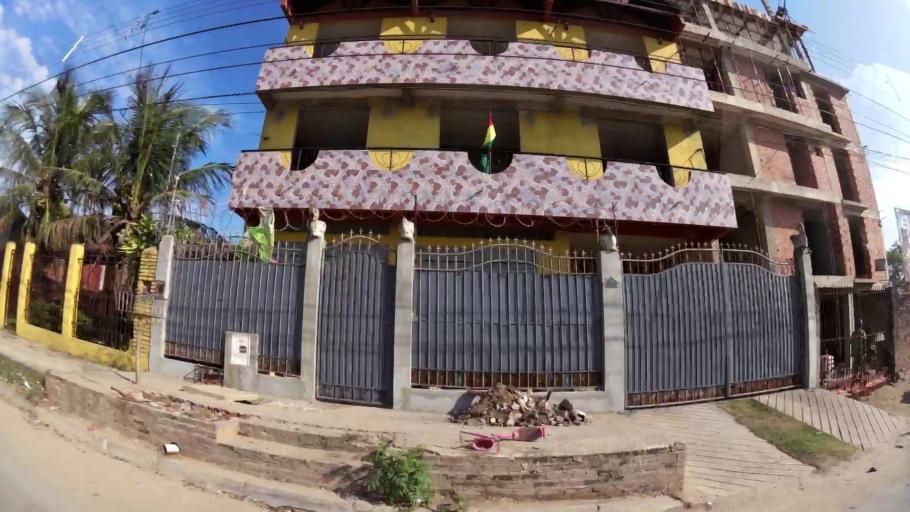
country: BO
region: Santa Cruz
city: Santa Cruz de la Sierra
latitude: -17.7355
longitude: -63.1420
